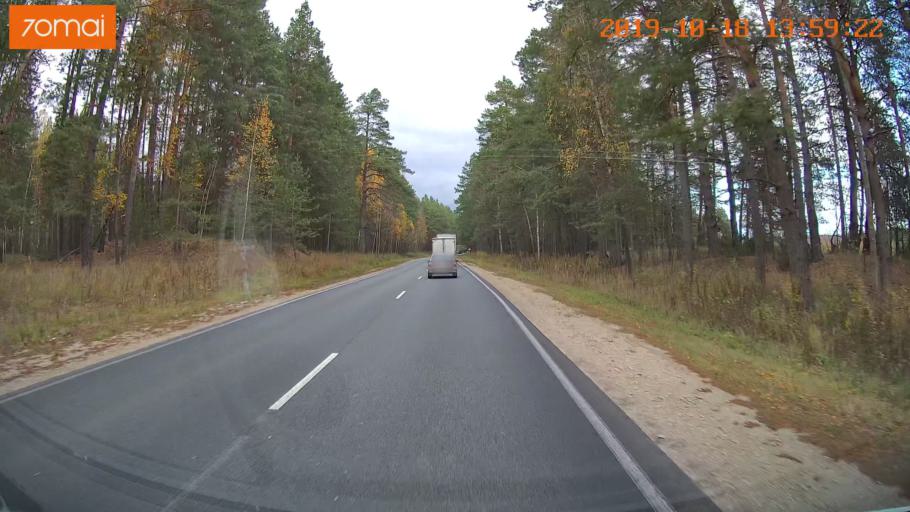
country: RU
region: Rjazan
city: Spas-Klepiki
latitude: 55.0936
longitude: 40.0630
